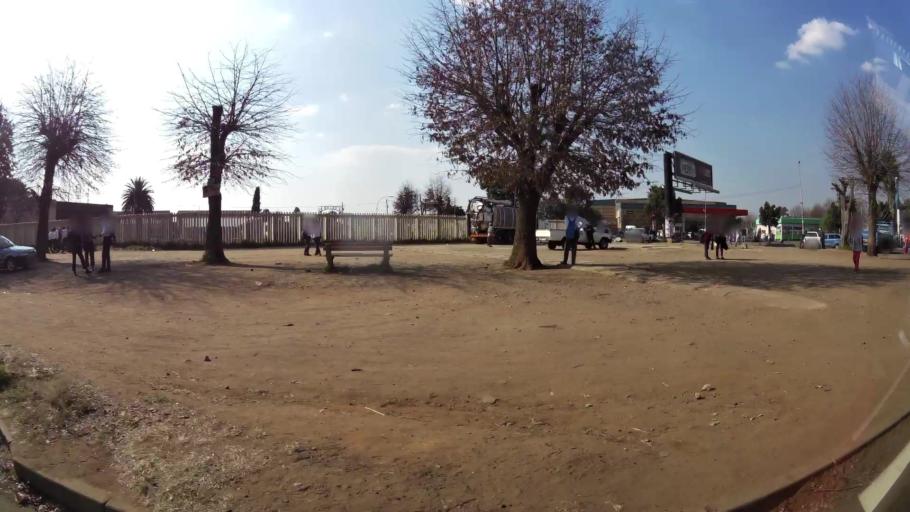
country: ZA
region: Gauteng
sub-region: Ekurhuleni Metropolitan Municipality
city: Brakpan
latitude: -26.1548
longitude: 28.4166
